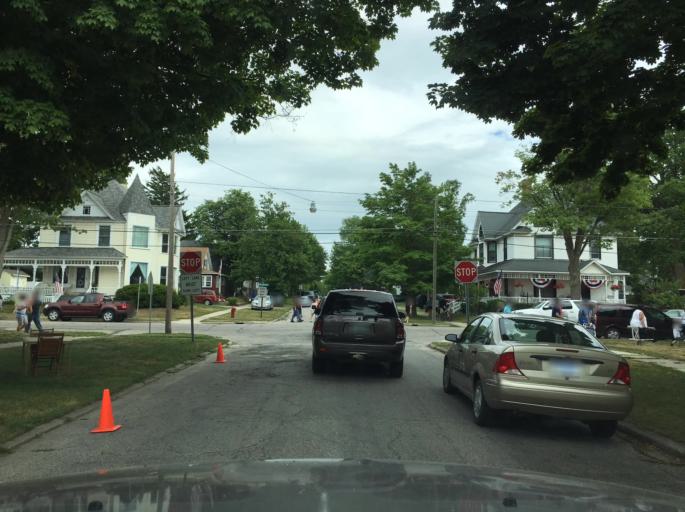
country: US
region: Michigan
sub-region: Mason County
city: Ludington
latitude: 43.9546
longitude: -86.4399
